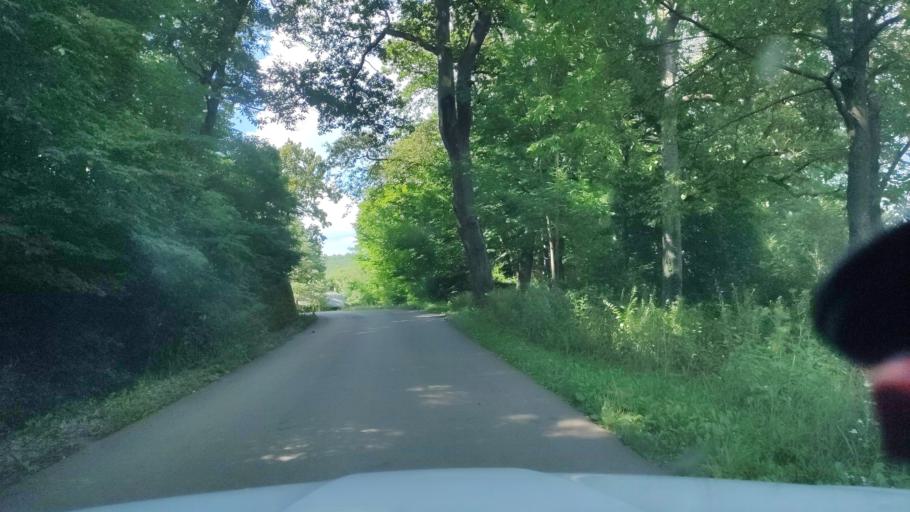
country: HU
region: Heves
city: Parad
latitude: 47.9225
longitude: 20.0581
